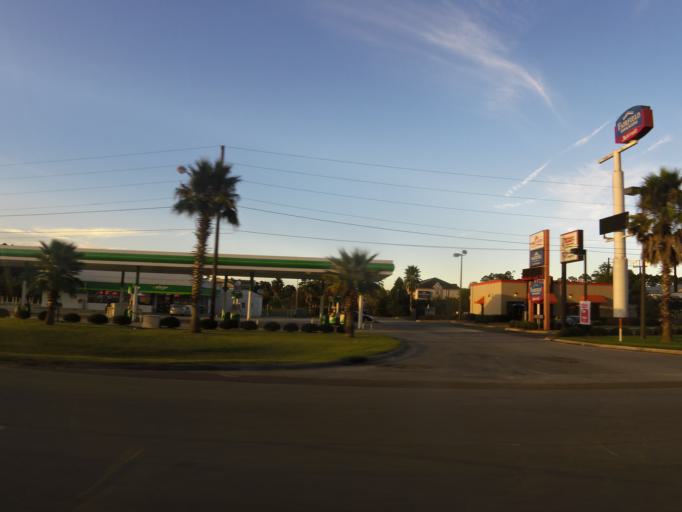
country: US
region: Georgia
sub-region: Camden County
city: Kingsland
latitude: 30.7897
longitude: -81.6554
